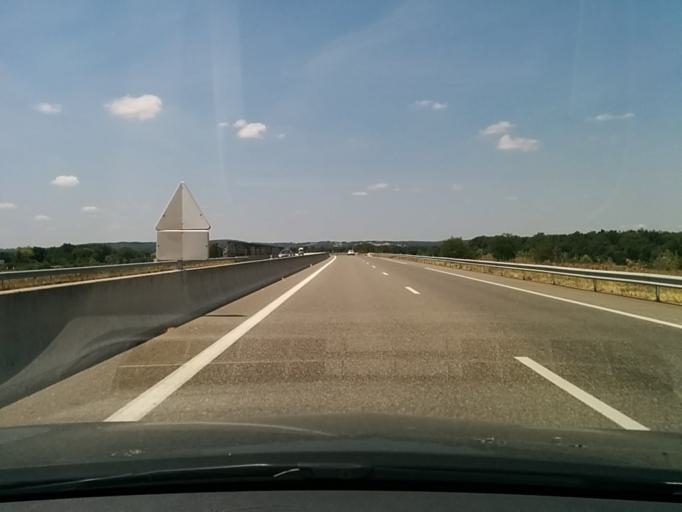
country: FR
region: Midi-Pyrenees
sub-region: Departement de la Haute-Garonne
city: Leguevin
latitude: 43.5819
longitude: 1.2206
